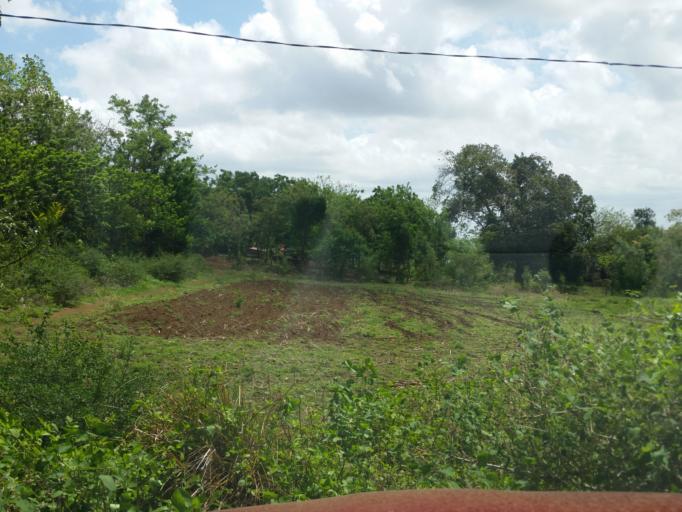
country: NI
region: Masaya
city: Ticuantepe
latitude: 12.0647
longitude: -86.2462
